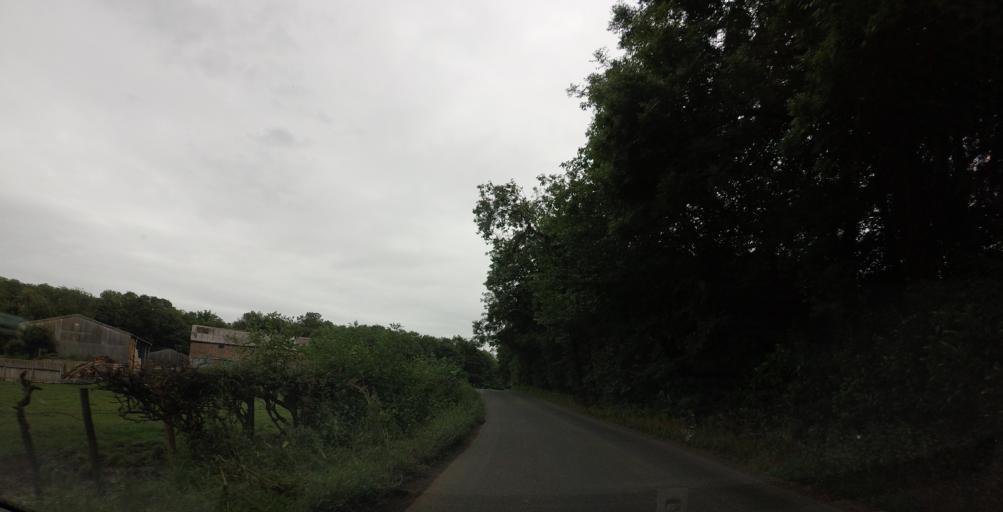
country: GB
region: England
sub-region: North Yorkshire
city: Ripon
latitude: 54.1012
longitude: -1.5154
